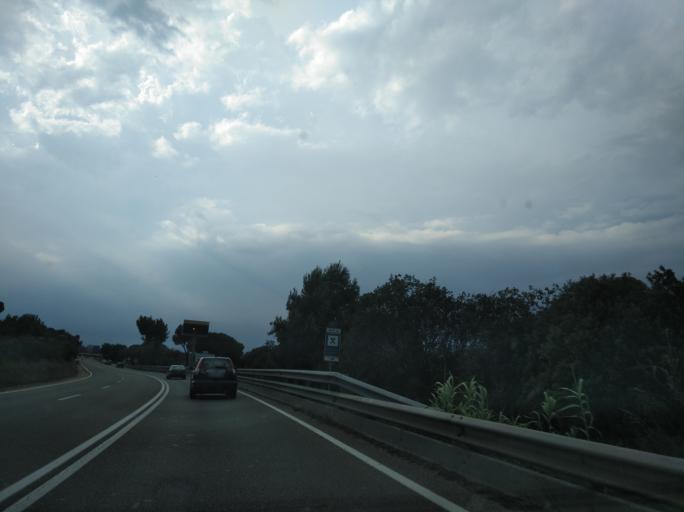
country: ES
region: Catalonia
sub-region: Provincia de Barcelona
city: Palafolls
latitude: 41.6660
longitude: 2.7312
